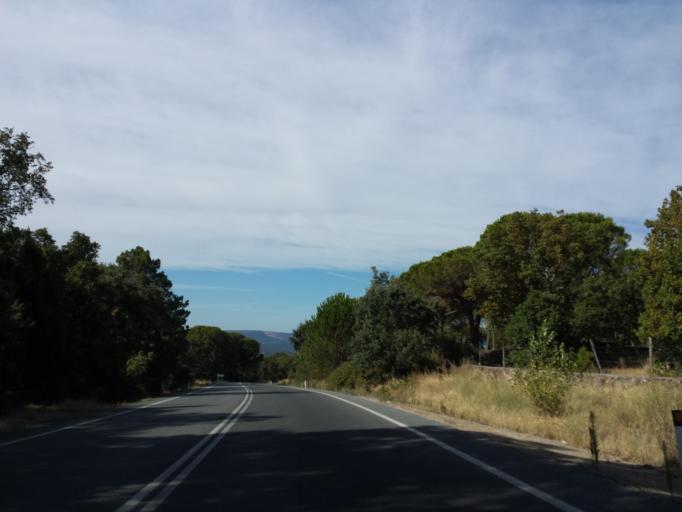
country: ES
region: Castille and Leon
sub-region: Provincia de Avila
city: Piedralaves
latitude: 40.3061
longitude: -4.7156
